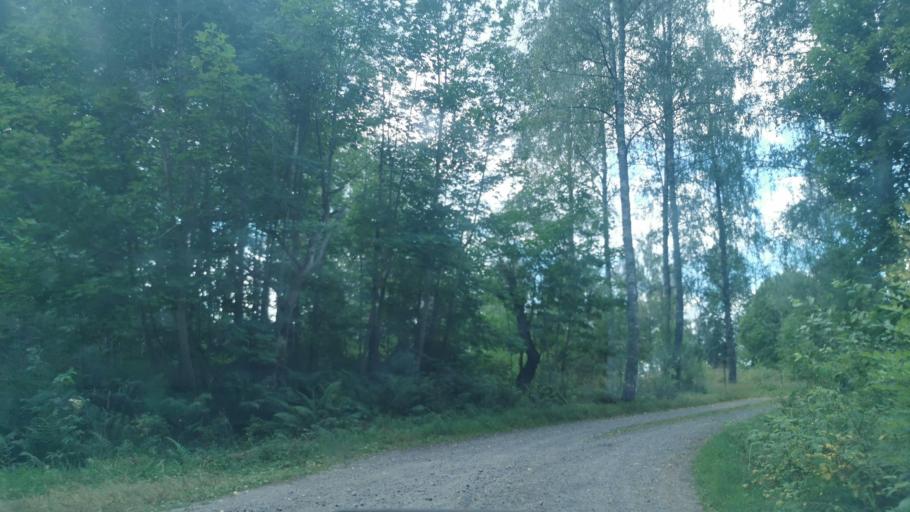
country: SE
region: OEstergoetland
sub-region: Finspangs Kommun
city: Finspang
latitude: 58.7988
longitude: 15.7798
